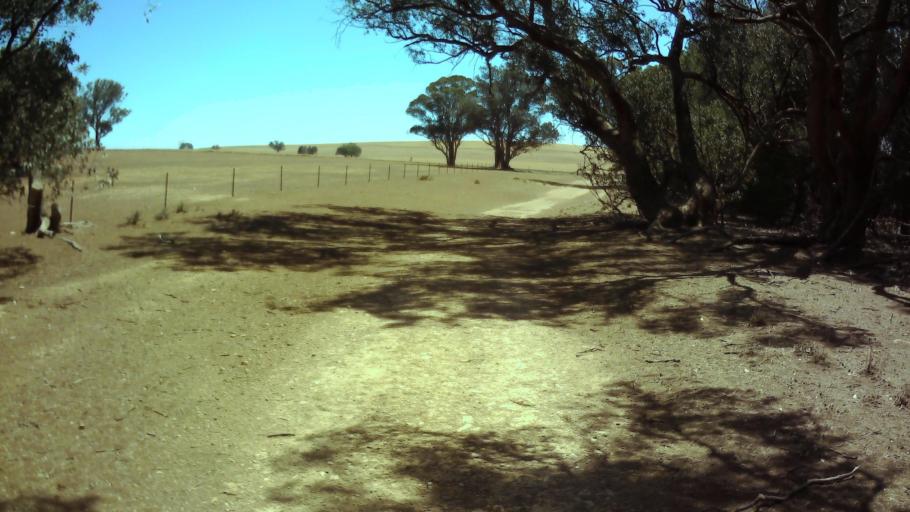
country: AU
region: New South Wales
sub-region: Weddin
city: Grenfell
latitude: -33.9835
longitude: 148.1642
